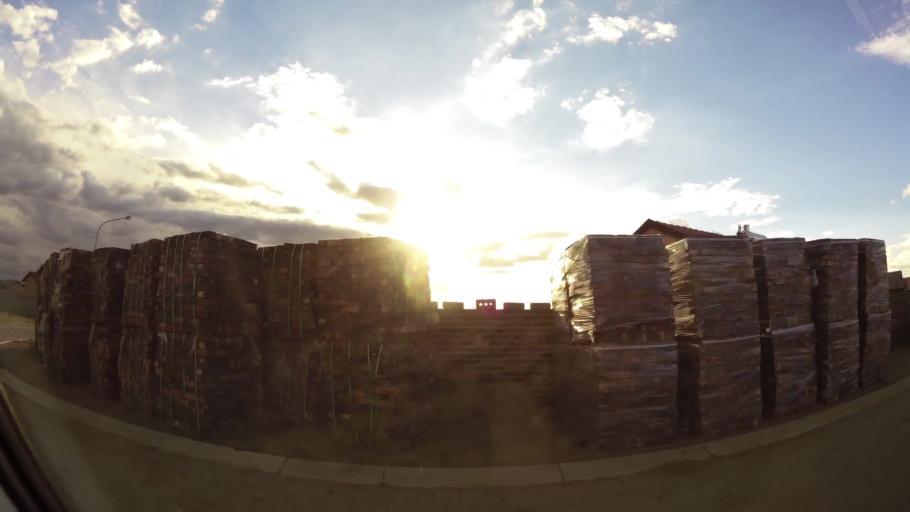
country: ZA
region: Limpopo
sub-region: Capricorn District Municipality
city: Polokwane
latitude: -23.9268
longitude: 29.4170
